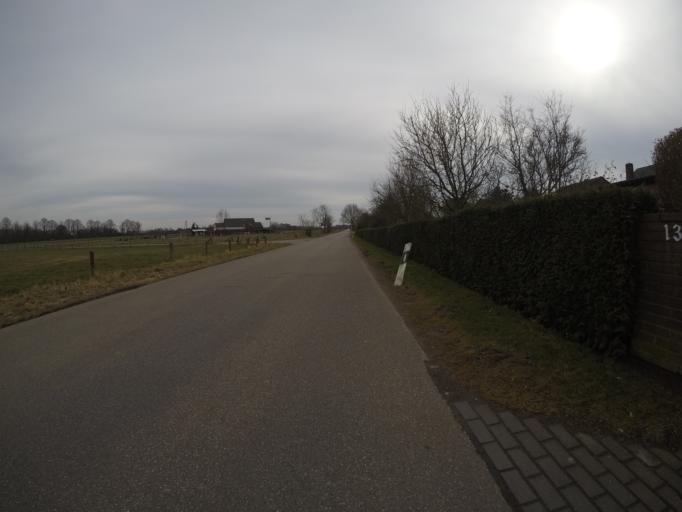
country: DE
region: North Rhine-Westphalia
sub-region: Regierungsbezirk Dusseldorf
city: Hamminkeln
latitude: 51.7596
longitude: 6.5803
